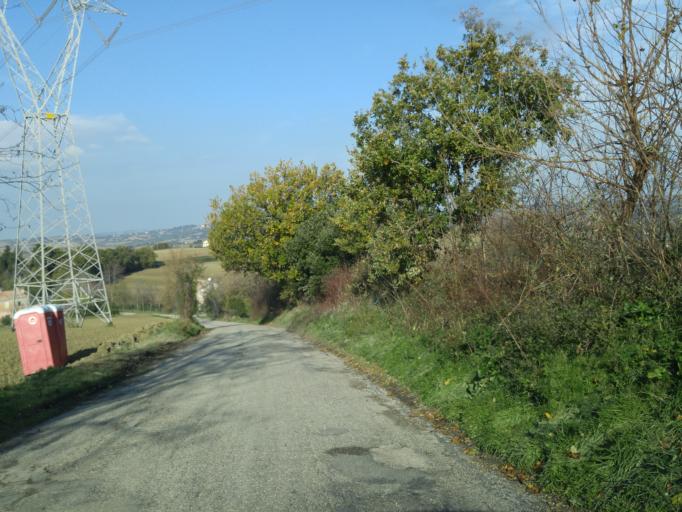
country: IT
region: The Marches
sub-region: Provincia di Pesaro e Urbino
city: Lucrezia
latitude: 43.8080
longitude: 12.9122
